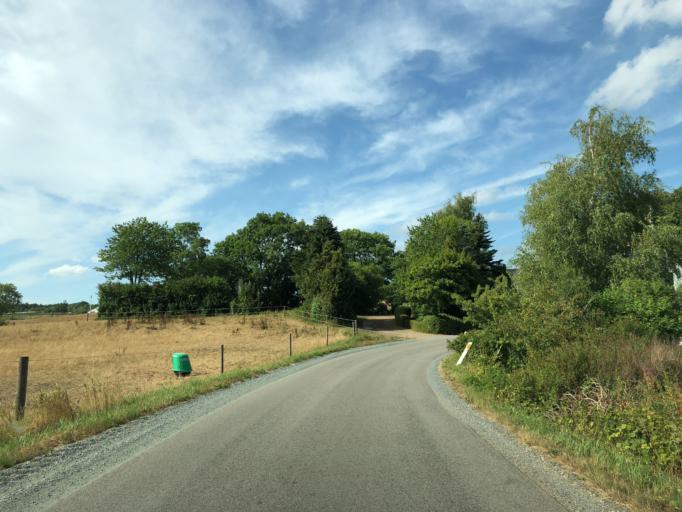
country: DK
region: South Denmark
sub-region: Vejle Kommune
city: Egtved
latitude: 55.6693
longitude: 9.3024
